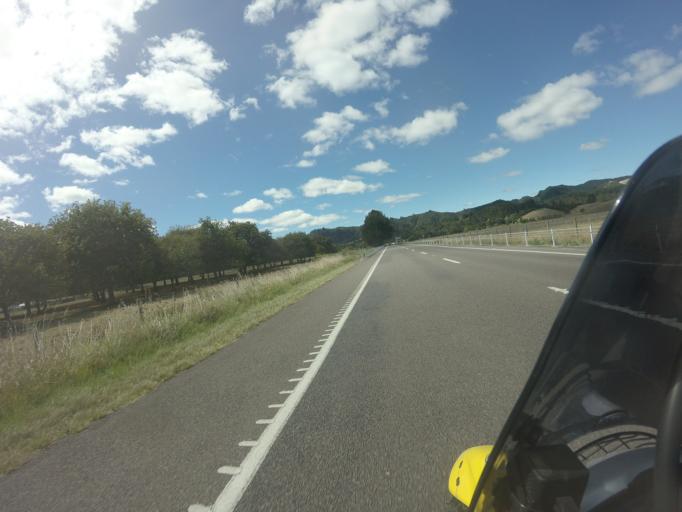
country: NZ
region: Bay of Plenty
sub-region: Whakatane District
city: Edgecumbe
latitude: -38.0228
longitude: 176.8406
